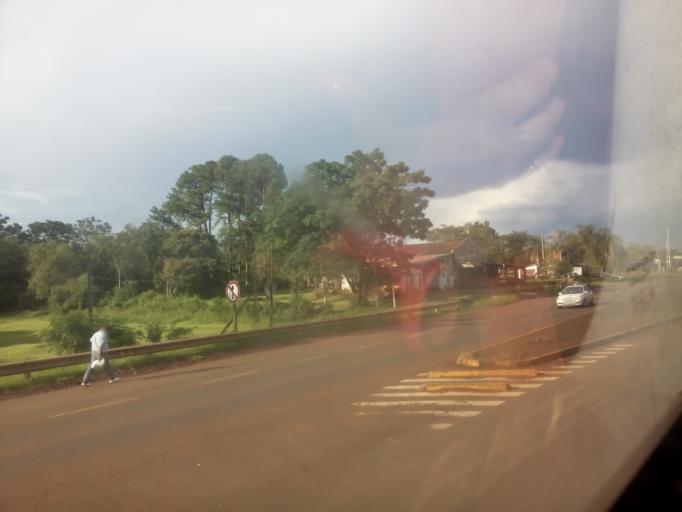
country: AR
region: Misiones
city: Santa Ana
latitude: -27.3778
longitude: -55.5774
